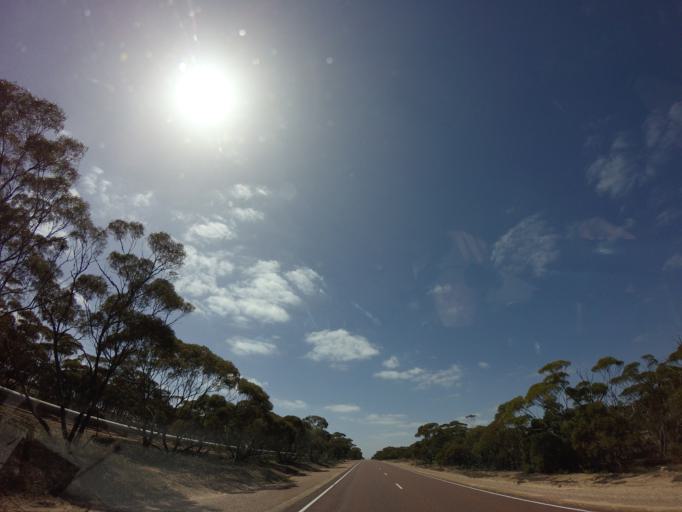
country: AU
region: South Australia
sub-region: Kimba
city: Caralue
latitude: -33.1077
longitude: 135.5279
